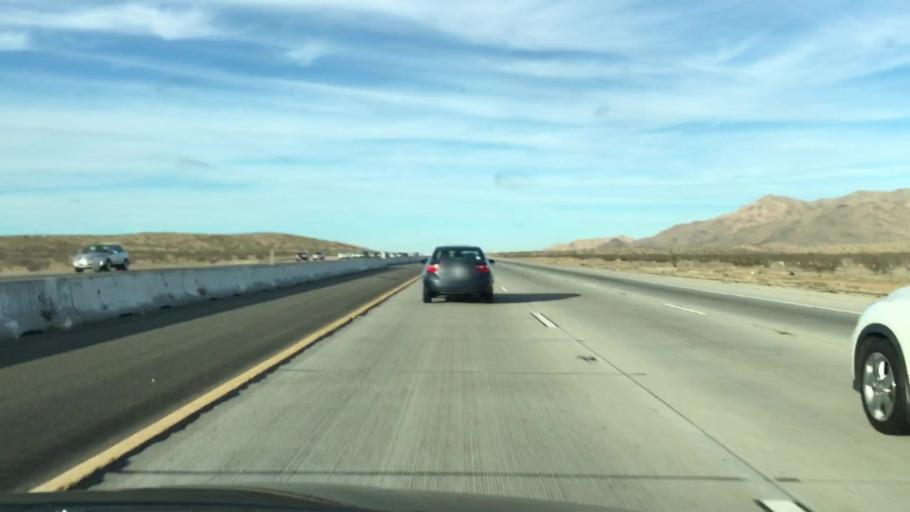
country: US
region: California
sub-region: San Bernardino County
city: Victorville
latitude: 34.6619
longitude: -117.2116
